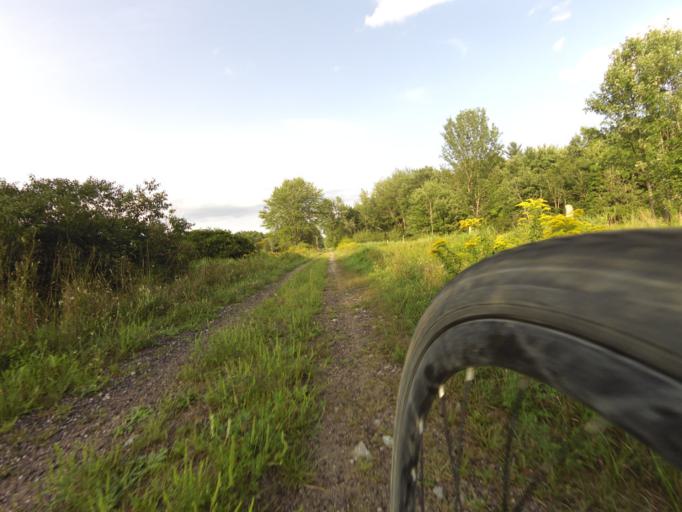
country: CA
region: Ontario
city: Kingston
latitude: 44.4998
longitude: -76.4419
